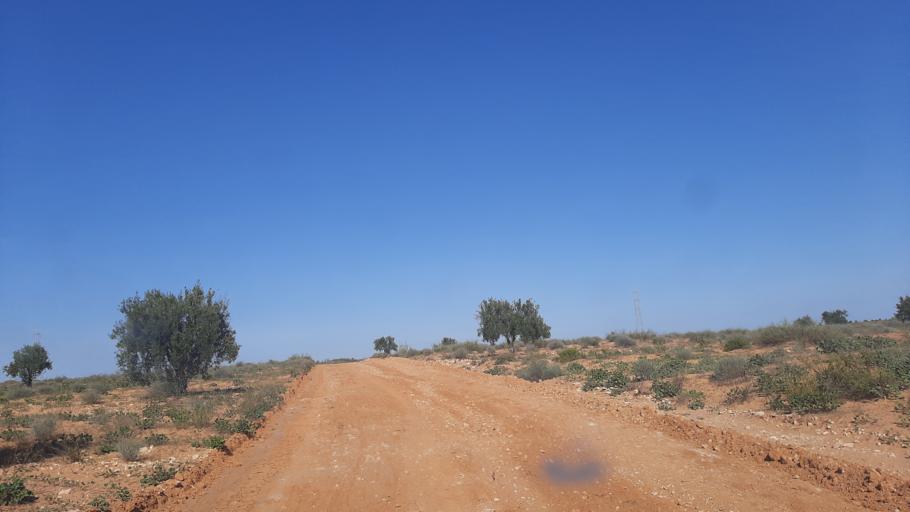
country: TN
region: Madanin
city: Medenine
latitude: 33.2752
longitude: 10.7718
